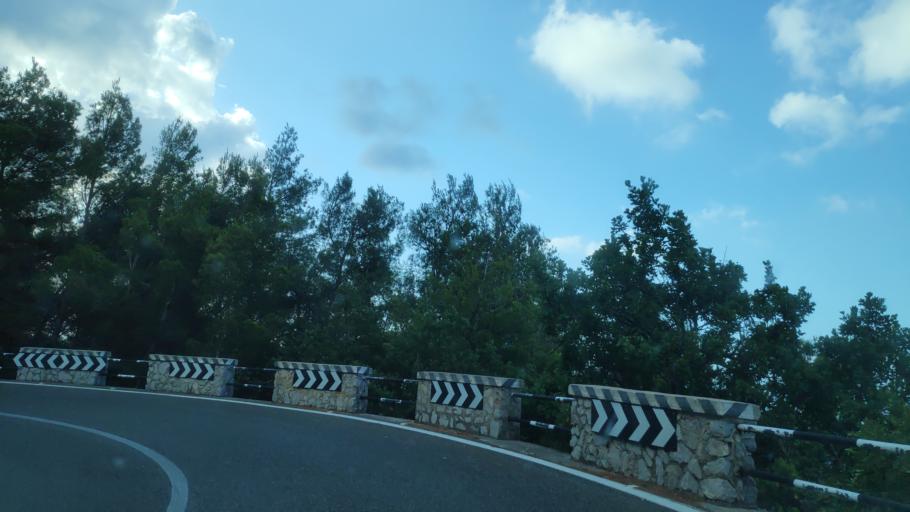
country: IT
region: Campania
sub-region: Provincia di Napoli
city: Arola-Preazzano
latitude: 40.6154
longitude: 14.4361
